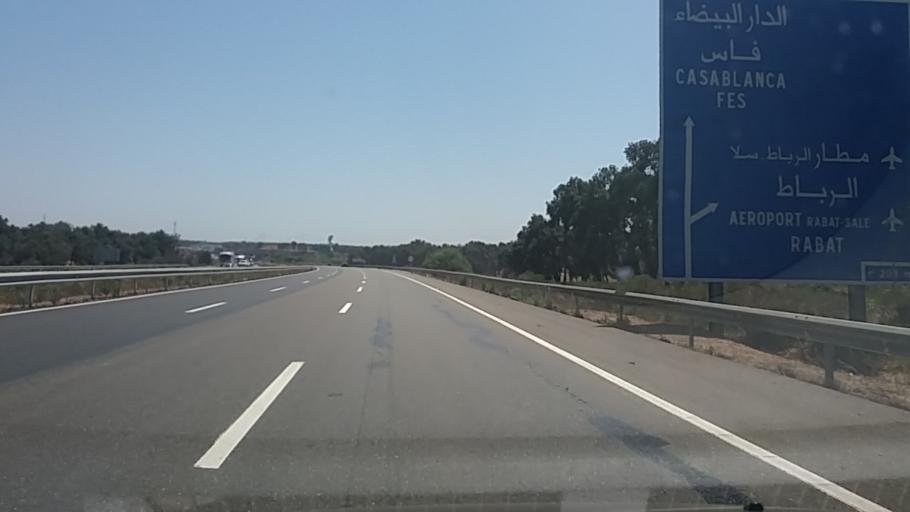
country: MA
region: Rabat-Sale-Zemmour-Zaer
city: Sale
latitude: 34.0336
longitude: -6.7124
